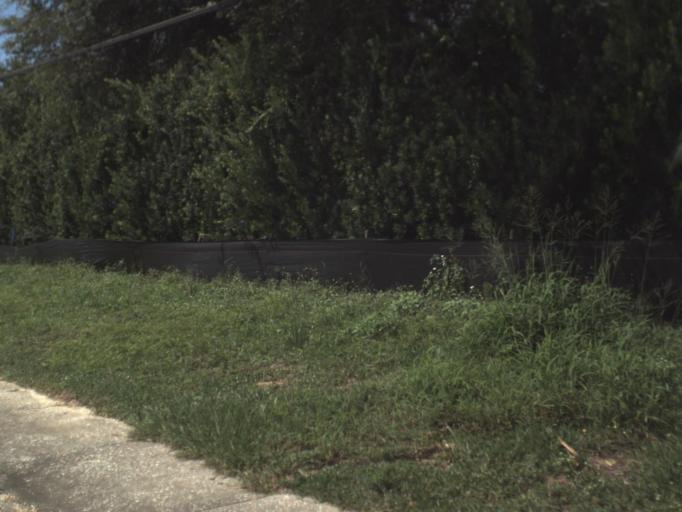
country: US
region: Florida
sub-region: Polk County
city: Haines City
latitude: 28.0969
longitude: -81.6233
